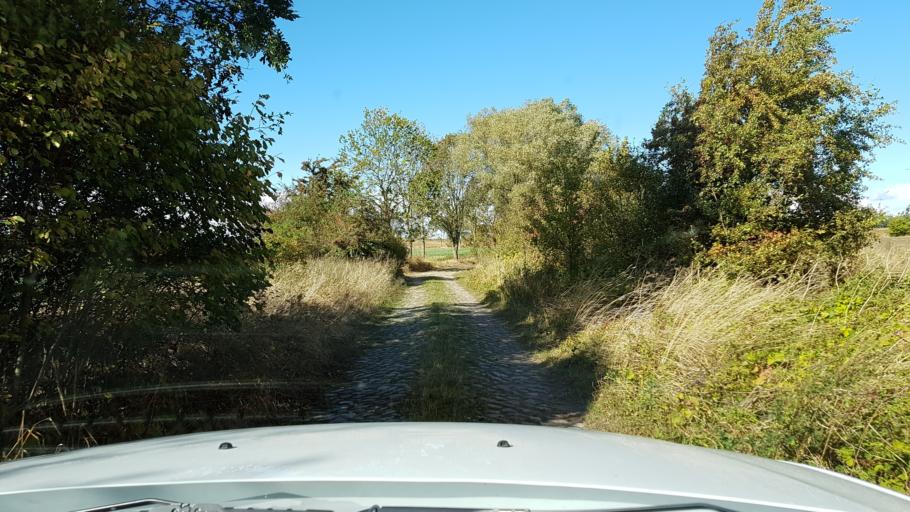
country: PL
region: West Pomeranian Voivodeship
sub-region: Powiat gryfinski
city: Banie
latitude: 53.1406
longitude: 14.6432
